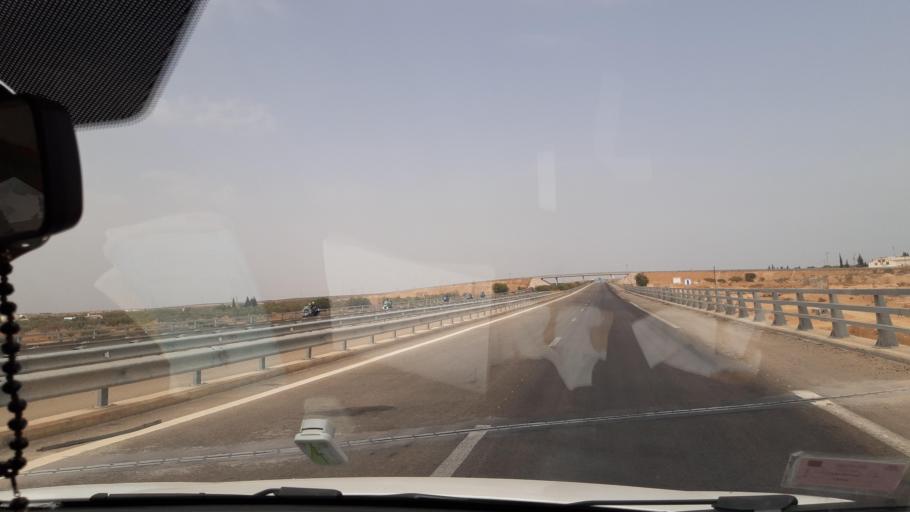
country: TN
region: Safaqis
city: Sfax
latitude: 34.8804
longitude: 10.7034
